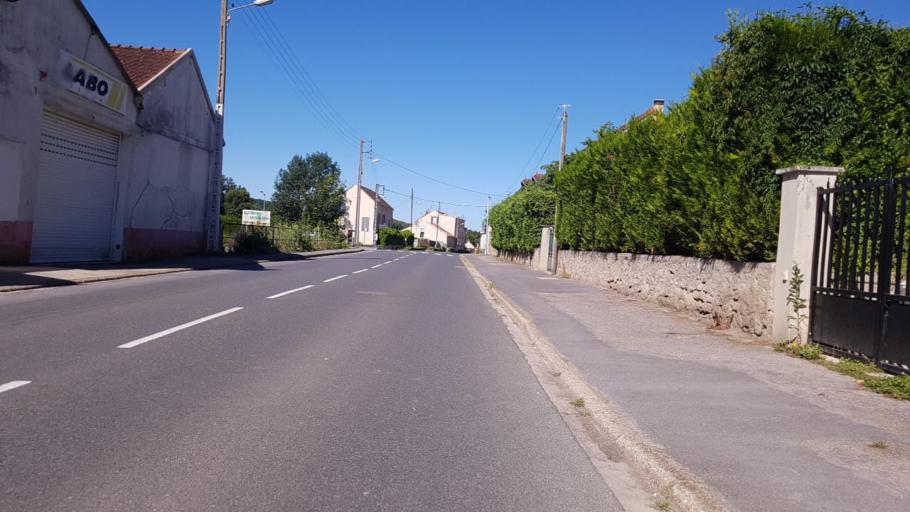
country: FR
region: Picardie
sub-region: Departement de l'Aisne
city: Charly-sur-Marne
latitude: 48.9721
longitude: 3.3220
